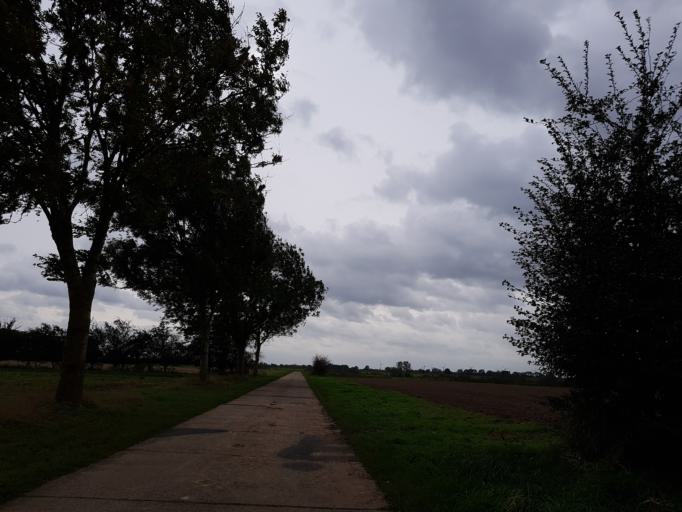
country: DE
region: Lower Saxony
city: Ahsen-Oetzen
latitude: 52.9857
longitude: 9.0689
